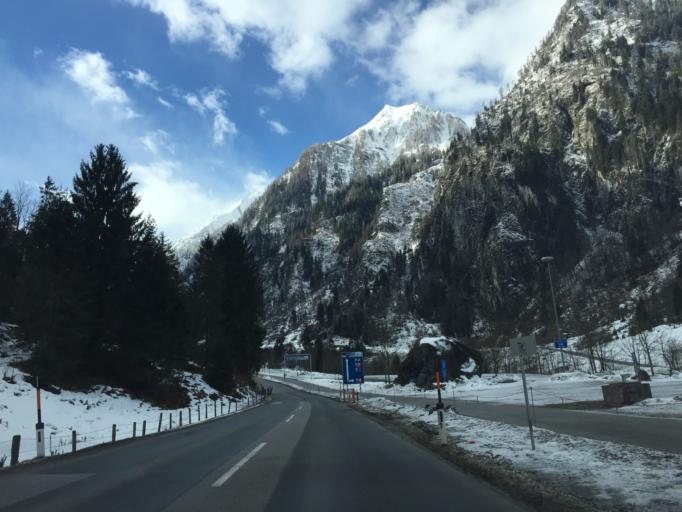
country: AT
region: Salzburg
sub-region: Politischer Bezirk Zell am See
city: Kaprun
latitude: 47.2342
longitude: 12.7293
